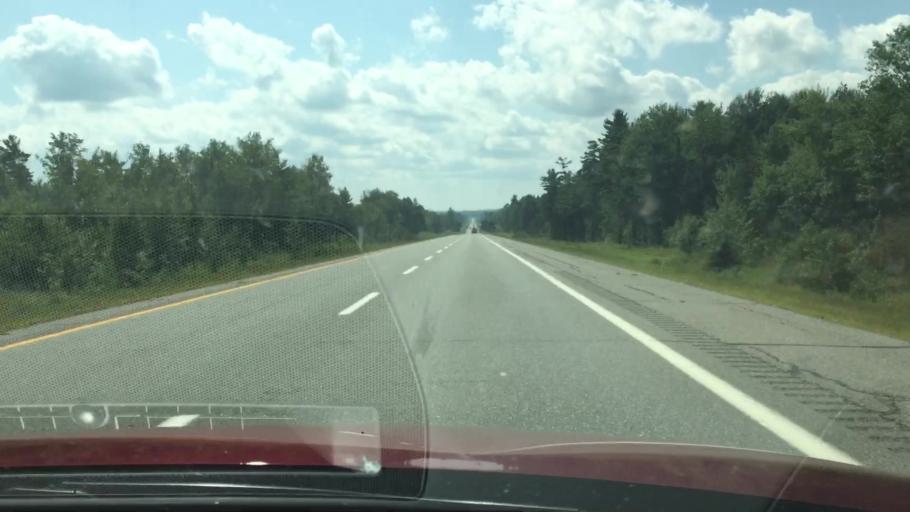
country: US
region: Maine
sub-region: Penobscot County
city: Enfield
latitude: 45.3436
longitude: -68.6196
